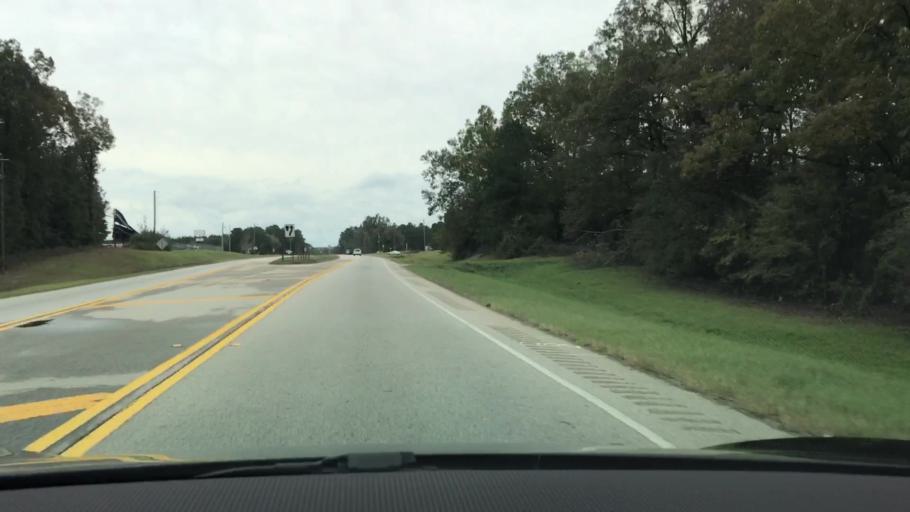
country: US
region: Georgia
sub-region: Jefferson County
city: Louisville
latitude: 32.9880
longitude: -82.3928
